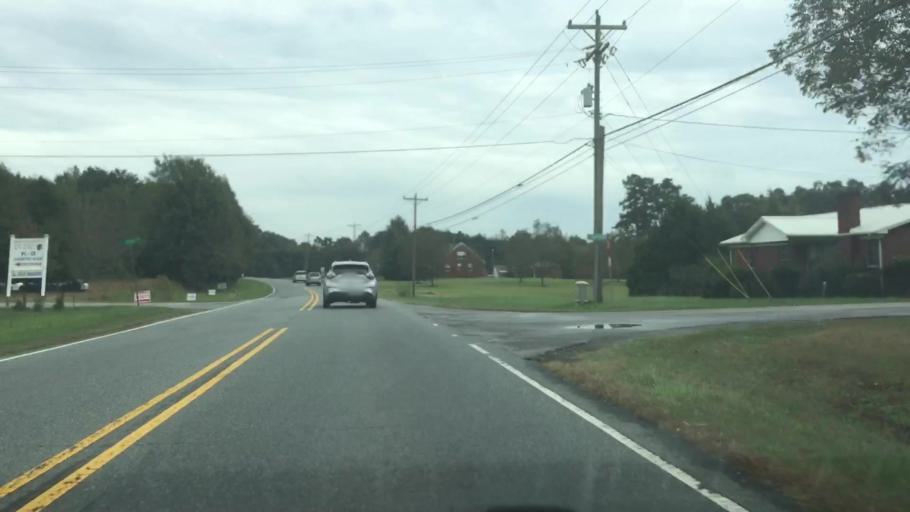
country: US
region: North Carolina
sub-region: Iredell County
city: Mooresville
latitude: 35.6401
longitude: -80.8369
